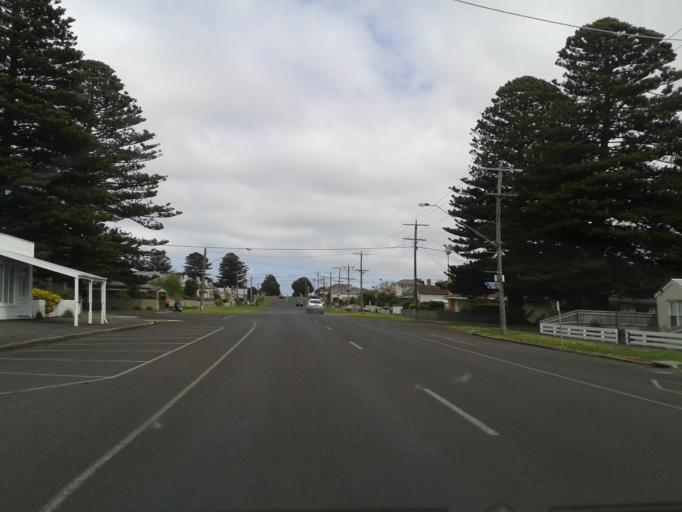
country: AU
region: Victoria
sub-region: Moyne
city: Port Fairy
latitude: -38.3830
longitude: 142.2325
